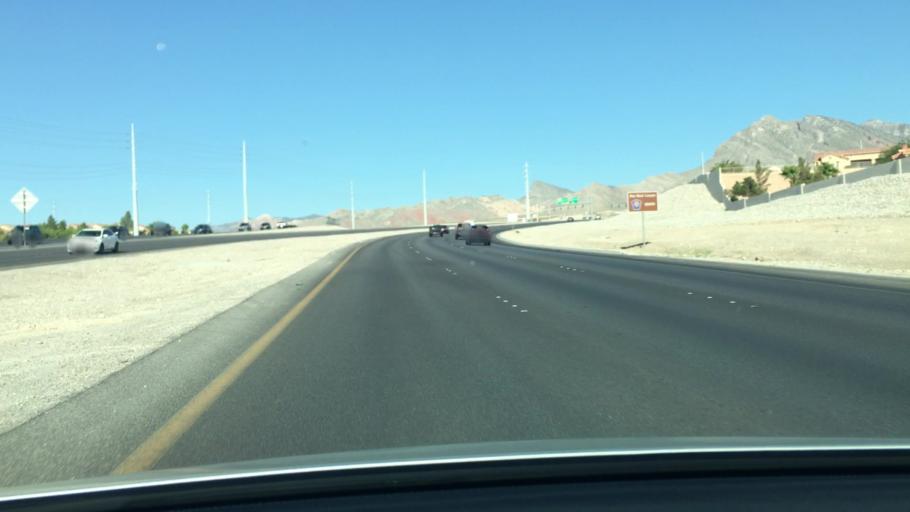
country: US
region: Nevada
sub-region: Clark County
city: Summerlin South
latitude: 36.1919
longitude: -115.3366
